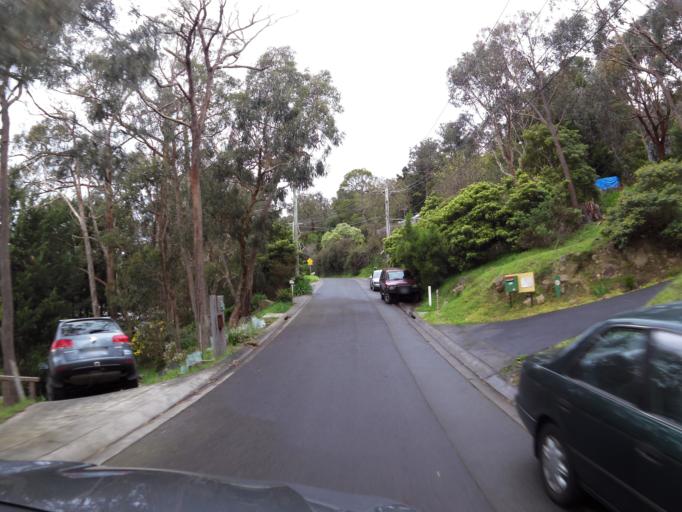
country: AU
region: Victoria
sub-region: Knox
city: The Basin
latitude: -37.8621
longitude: 145.3131
